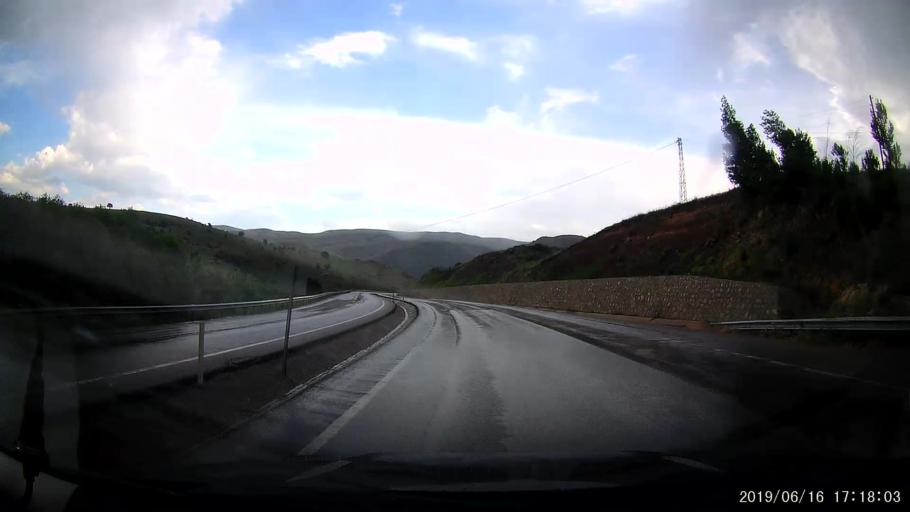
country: TR
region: Erzincan
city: Tercan
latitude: 39.8196
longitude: 40.5288
